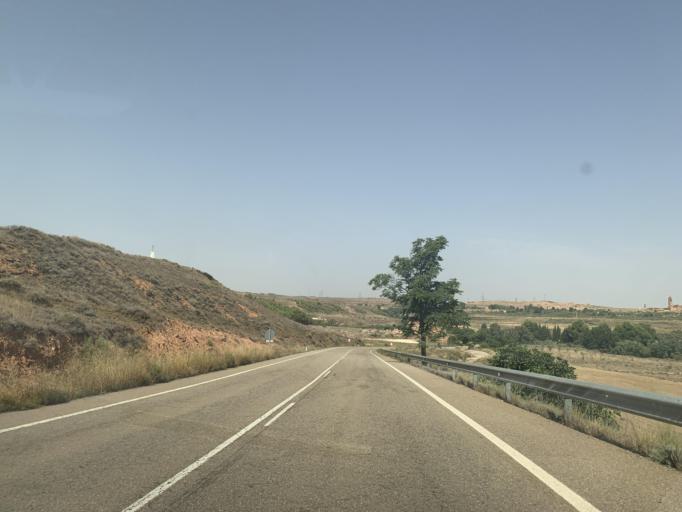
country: ES
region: Aragon
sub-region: Provincia de Zaragoza
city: Belchite
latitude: 41.2910
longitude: -0.7343
